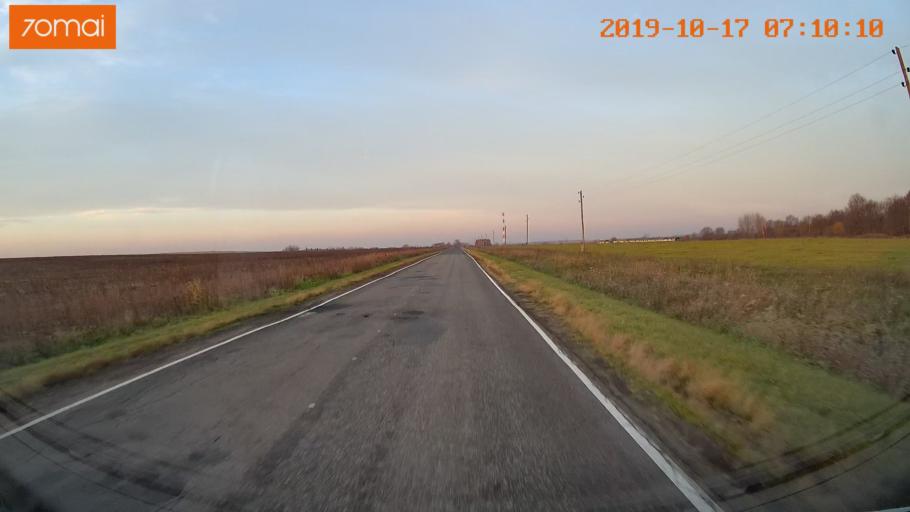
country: RU
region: Vladimir
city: Suzdal'
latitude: 56.4136
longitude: 40.3672
